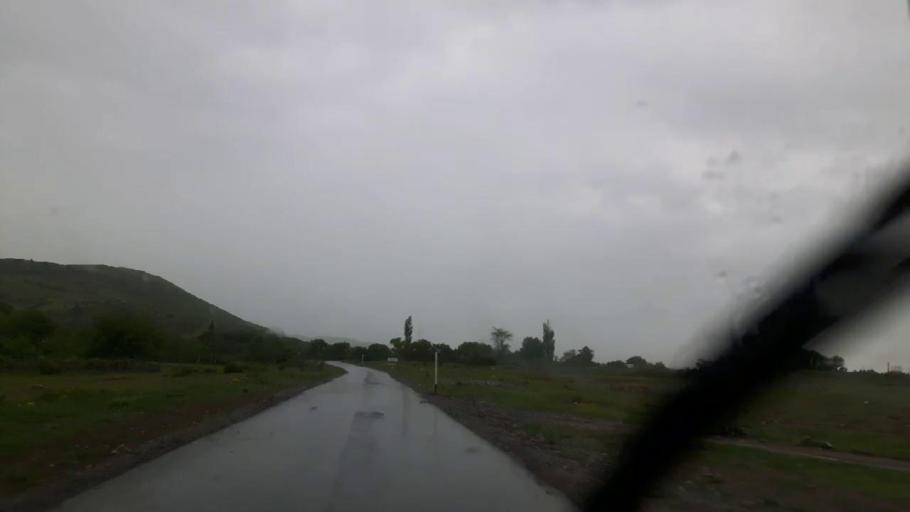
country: GE
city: Agara
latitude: 41.9817
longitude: 43.9446
